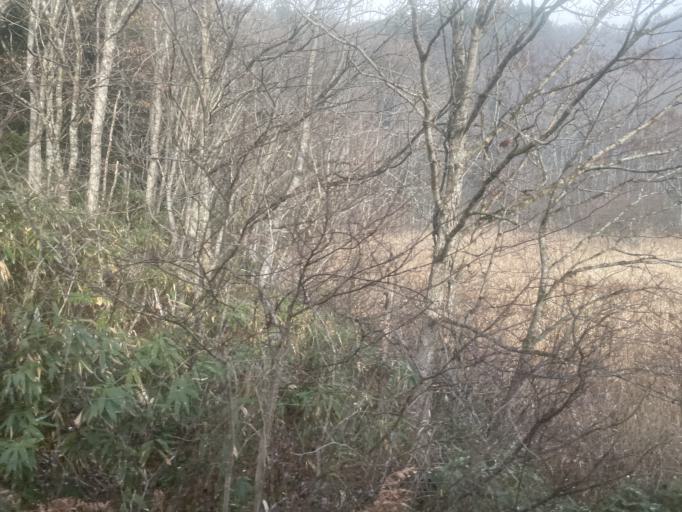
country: JP
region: Aomori
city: Goshogawara
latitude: 41.0817
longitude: 140.5232
